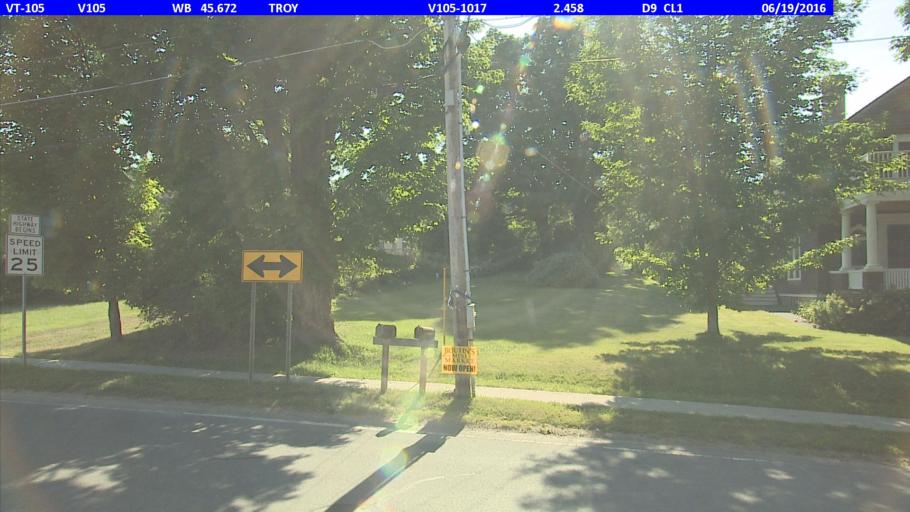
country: US
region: Vermont
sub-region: Orleans County
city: Newport
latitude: 44.9936
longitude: -72.4077
